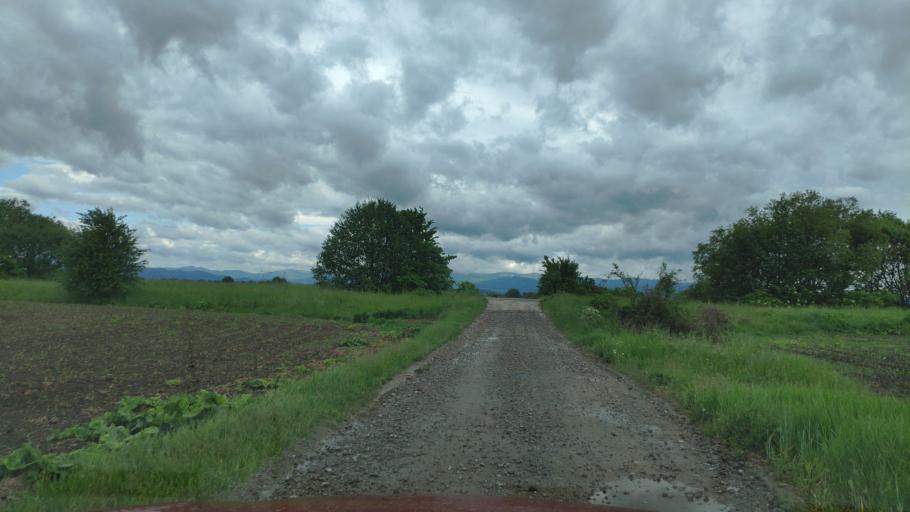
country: SK
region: Kosicky
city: Moldava nad Bodvou
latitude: 48.5561
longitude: 21.1160
